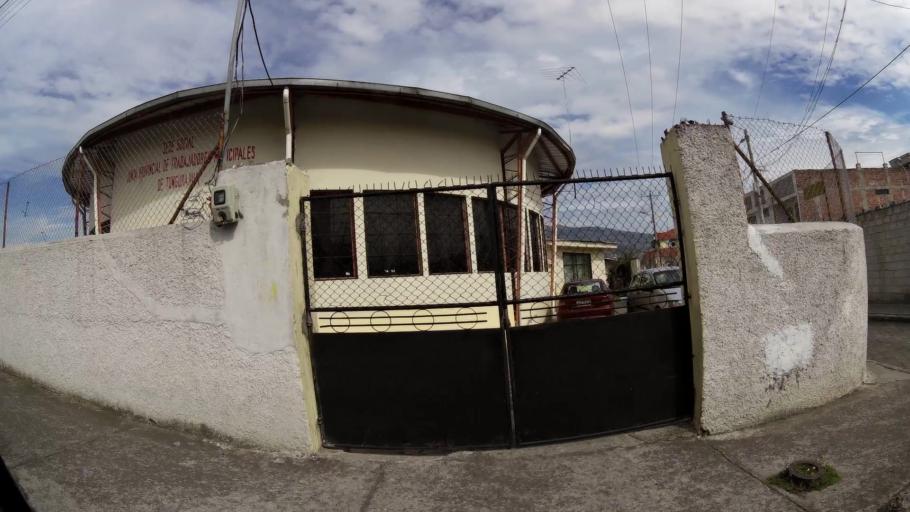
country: EC
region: Tungurahua
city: Ambato
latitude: -1.2486
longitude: -78.6287
